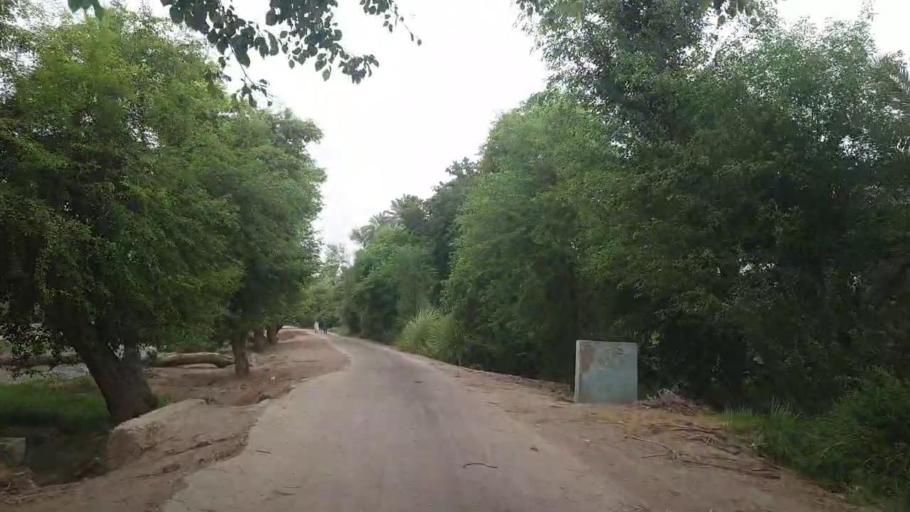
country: PK
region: Sindh
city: Khairpur
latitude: 27.5996
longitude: 68.7570
